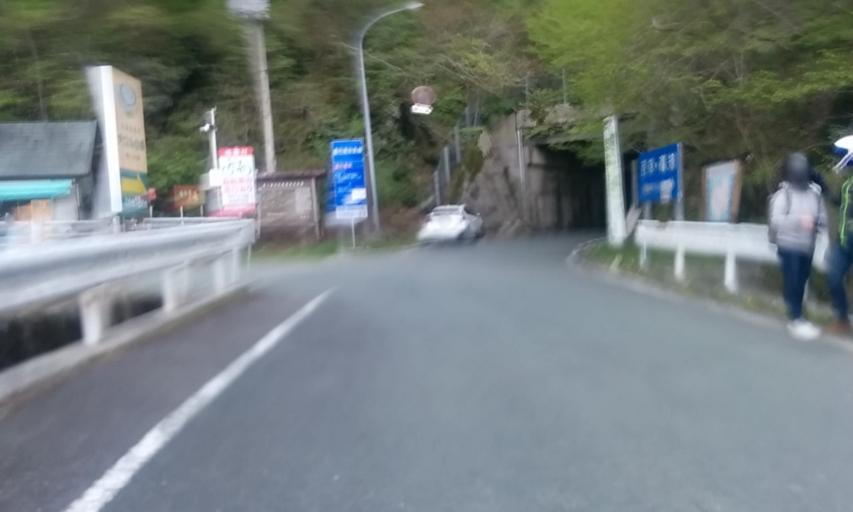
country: JP
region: Ehime
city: Saijo
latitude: 33.8000
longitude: 133.2665
